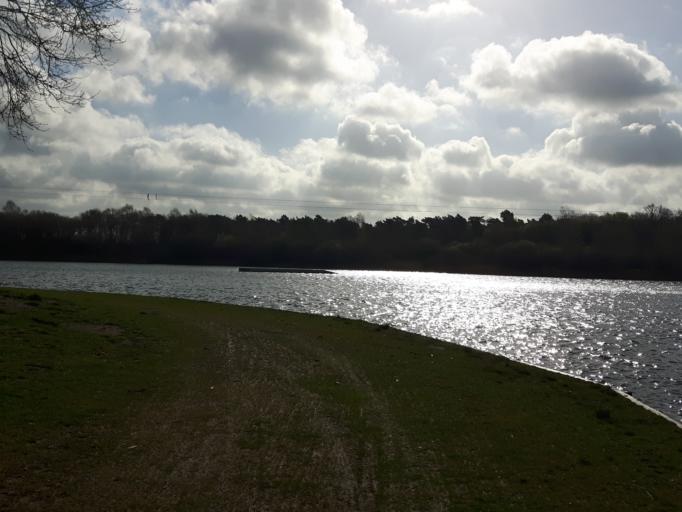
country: NL
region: Overijssel
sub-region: Gemeente Enschede
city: Enschede
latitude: 52.1805
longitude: 6.8405
